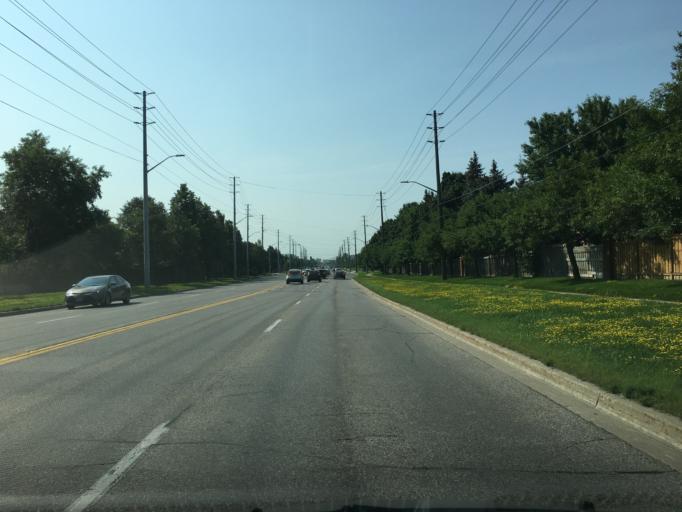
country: CA
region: Ontario
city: Markham
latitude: 43.8621
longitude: -79.3356
